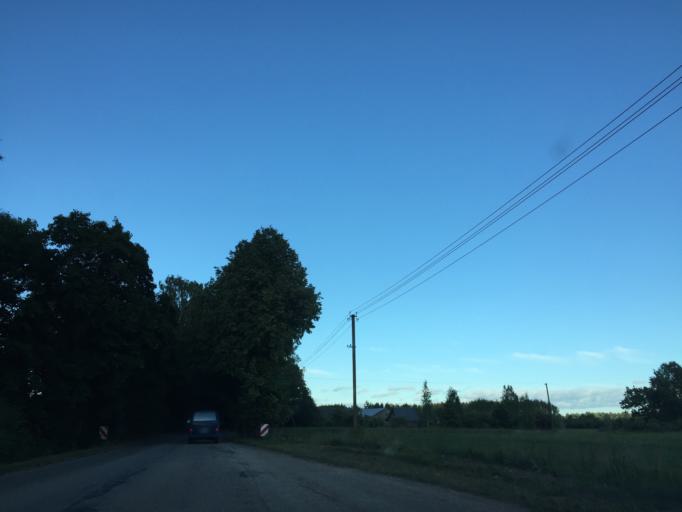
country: LV
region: Plavinu
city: Plavinas
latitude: 56.6098
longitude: 25.8113
